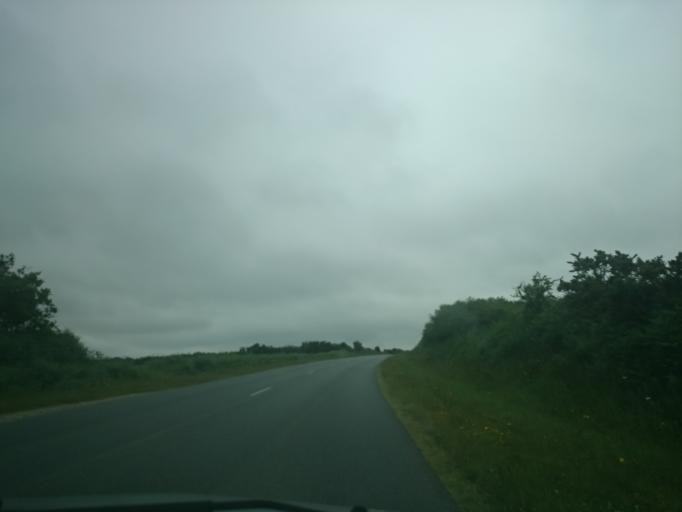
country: FR
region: Brittany
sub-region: Departement du Finistere
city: Saint-Pabu
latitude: 48.5511
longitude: -4.6094
